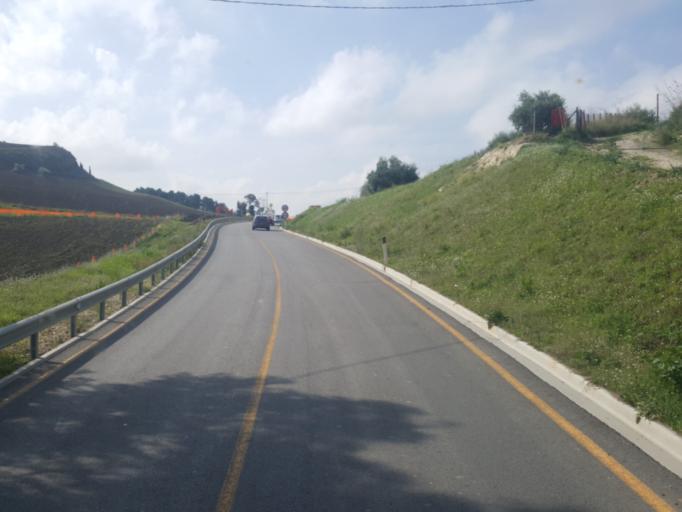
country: IT
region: Sicily
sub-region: Provincia di Caltanissetta
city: San Cataldo
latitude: 37.4492
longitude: 13.9587
